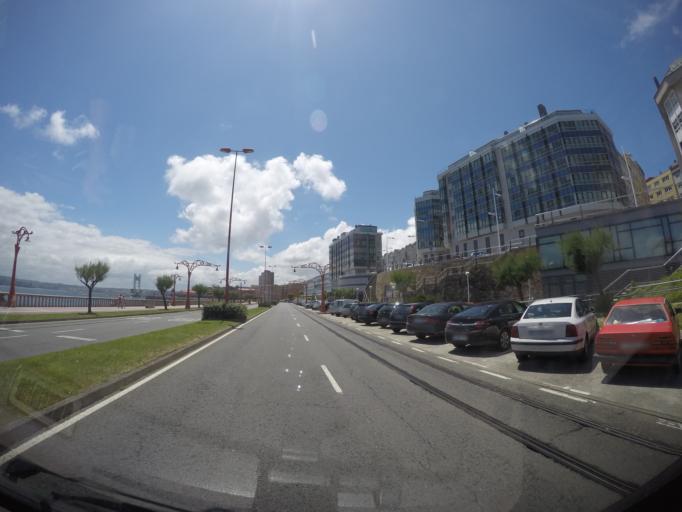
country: ES
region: Galicia
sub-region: Provincia da Coruna
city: A Coruna
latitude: 43.3731
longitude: -8.3906
